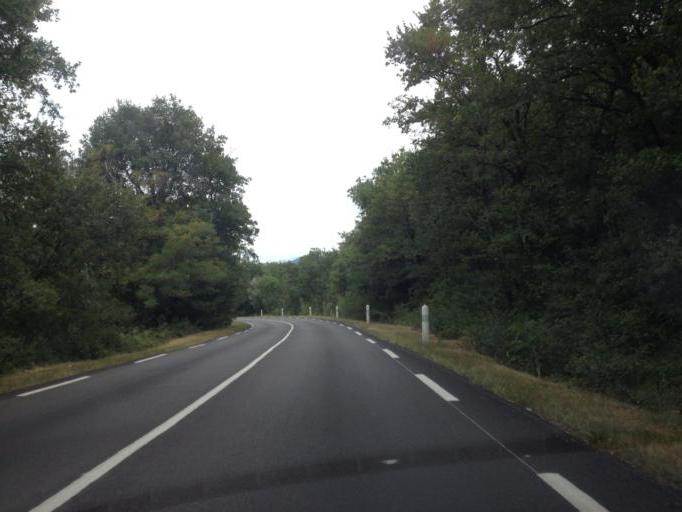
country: FR
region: Rhone-Alpes
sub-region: Departement de la Drome
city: Montelimar
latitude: 44.5304
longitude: 4.7673
